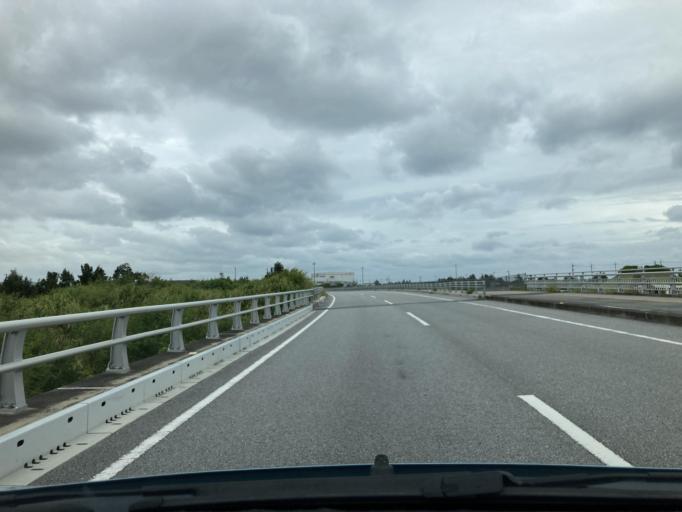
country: JP
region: Okinawa
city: Ginowan
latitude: 26.2141
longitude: 127.7706
